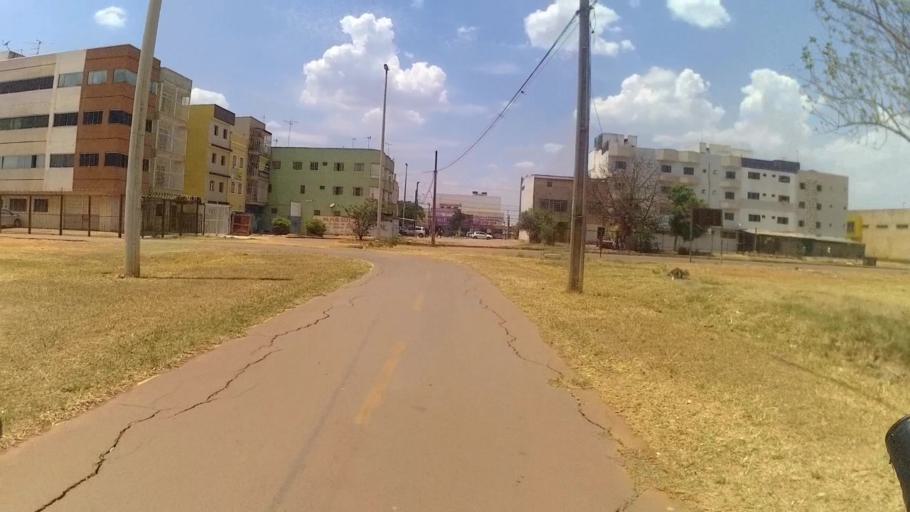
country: BR
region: Federal District
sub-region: Brasilia
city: Brasilia
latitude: -15.8709
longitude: -48.0708
